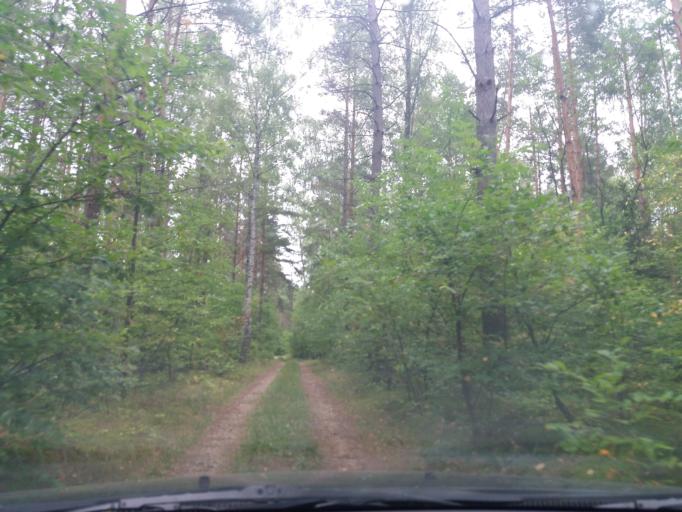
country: PL
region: Masovian Voivodeship
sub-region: Powiat mlawski
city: Wieczfnia Koscielna
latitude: 53.2295
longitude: 20.4752
